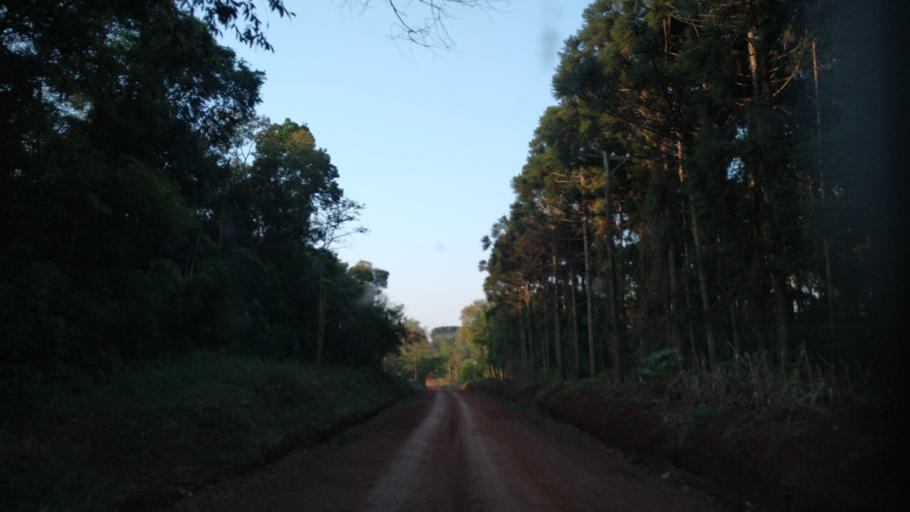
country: AR
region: Misiones
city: Jardin America
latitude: -27.0782
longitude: -55.2720
